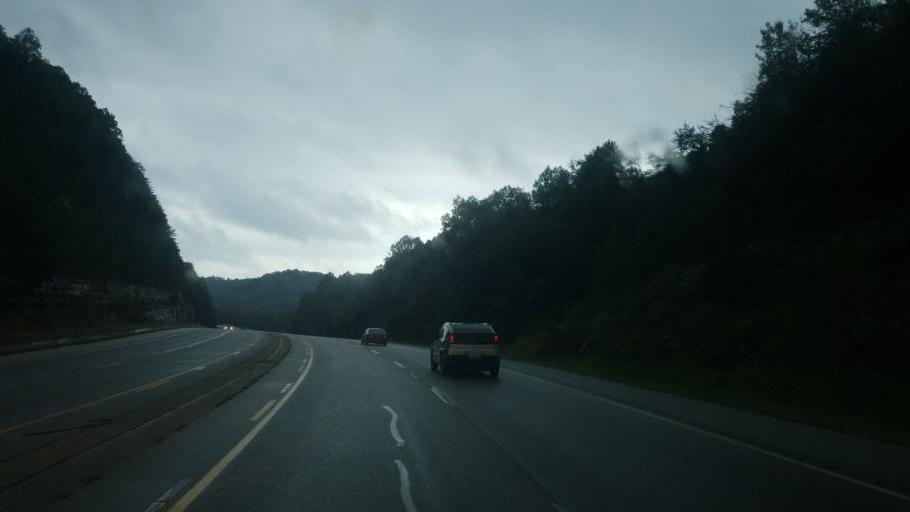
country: US
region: Kentucky
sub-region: Rowan County
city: Morehead
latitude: 38.1806
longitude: -83.4669
